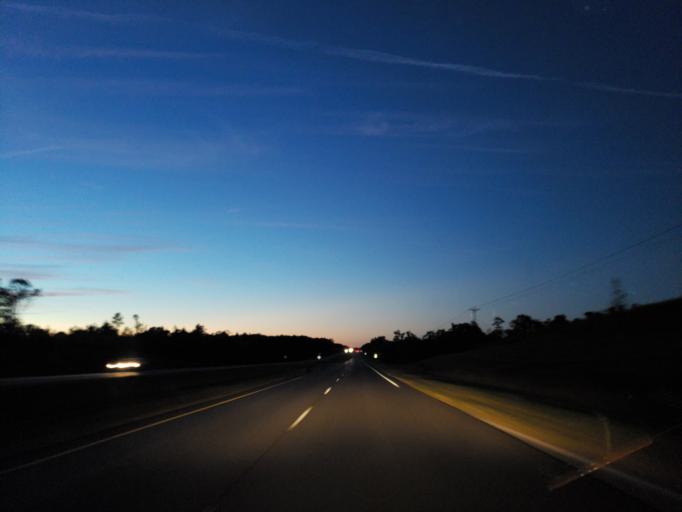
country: US
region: Mississippi
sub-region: Clarke County
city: Quitman
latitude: 32.0665
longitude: -88.6820
